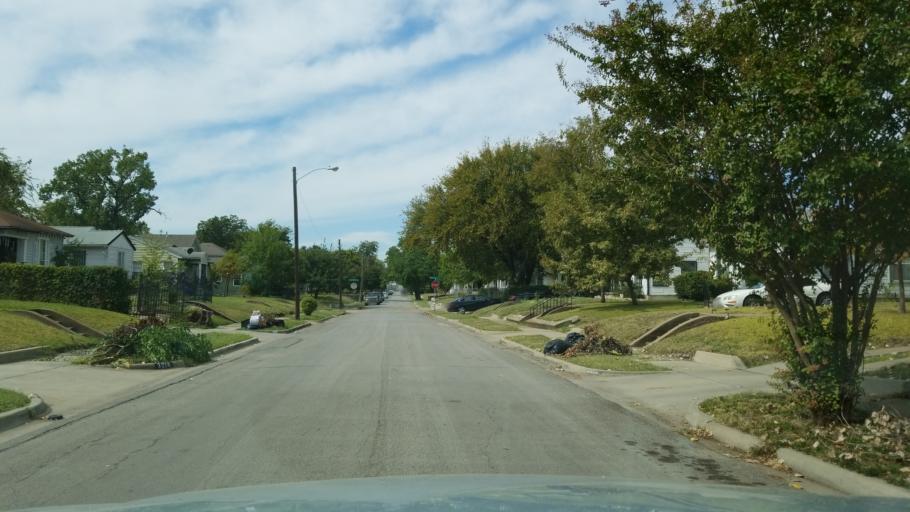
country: US
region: Texas
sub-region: Dallas County
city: Dallas
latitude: 32.7855
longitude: -96.7399
